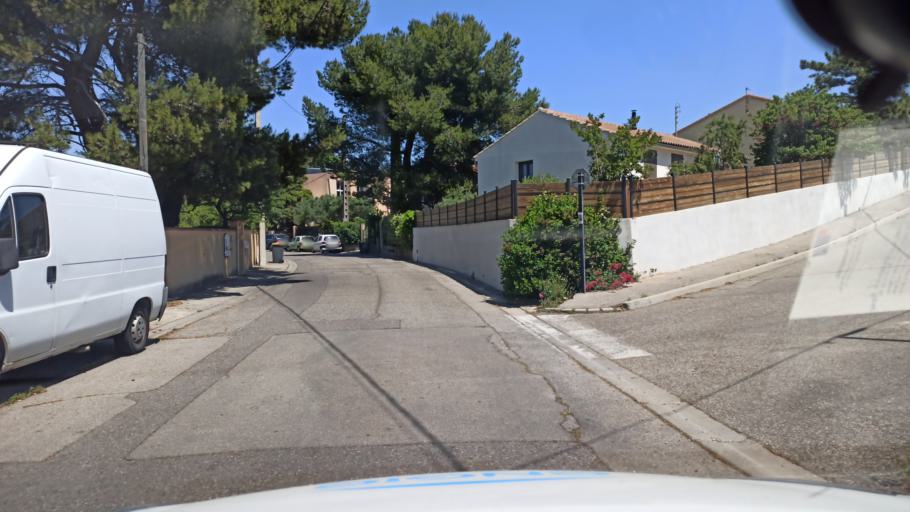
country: FR
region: Languedoc-Roussillon
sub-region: Departement du Gard
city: Les Angles
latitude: 43.9576
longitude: 4.7698
